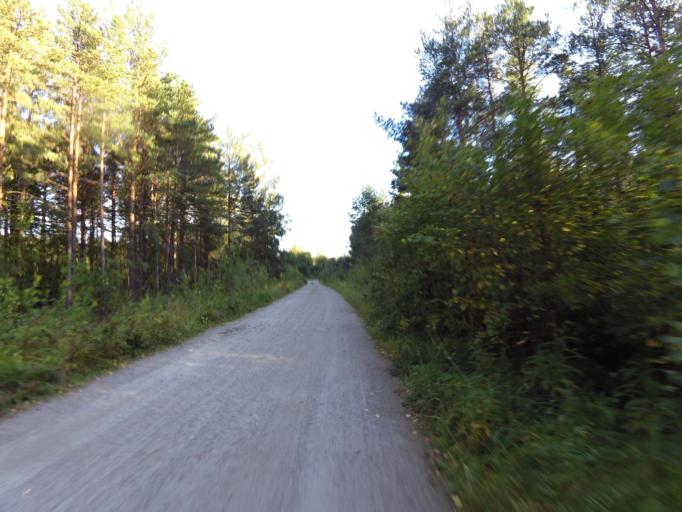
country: SE
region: Gaevleborg
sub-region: Gavle Kommun
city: Gavle
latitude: 60.6564
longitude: 17.1125
